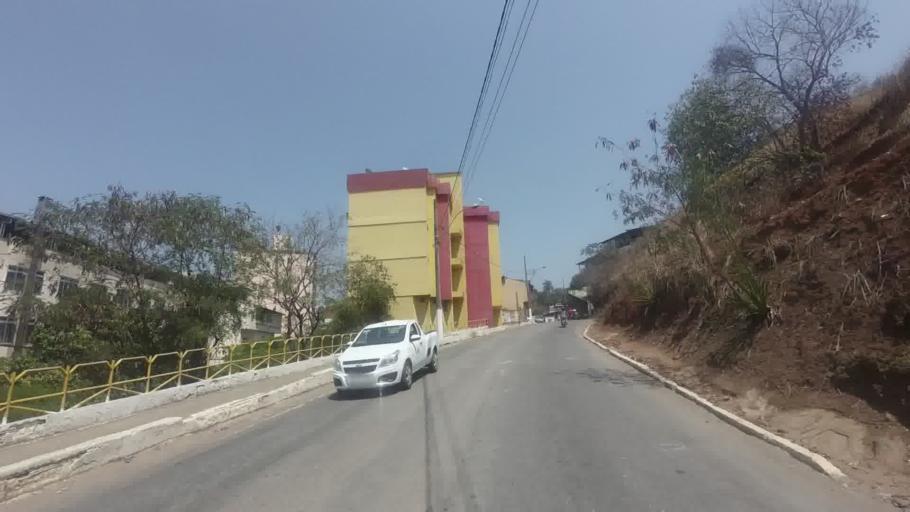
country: BR
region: Espirito Santo
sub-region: Cachoeiro De Itapemirim
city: Cachoeiro de Itapemirim
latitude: -20.8405
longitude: -41.1230
